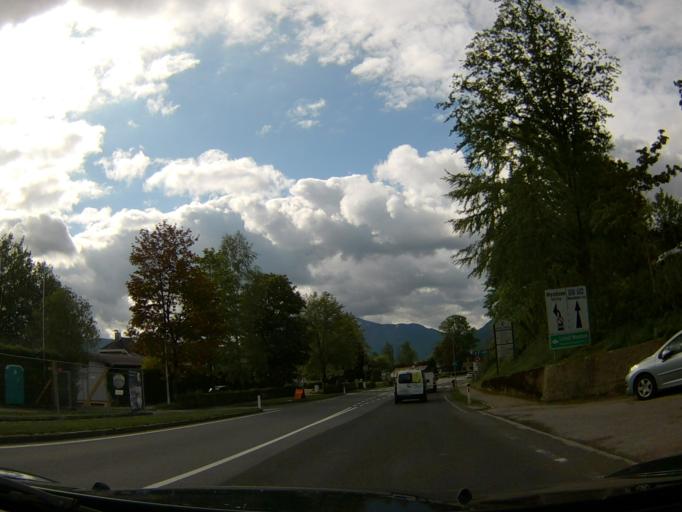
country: AT
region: Upper Austria
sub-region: Politischer Bezirk Vocklabruck
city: Mondsee
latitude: 47.8533
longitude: 13.3438
